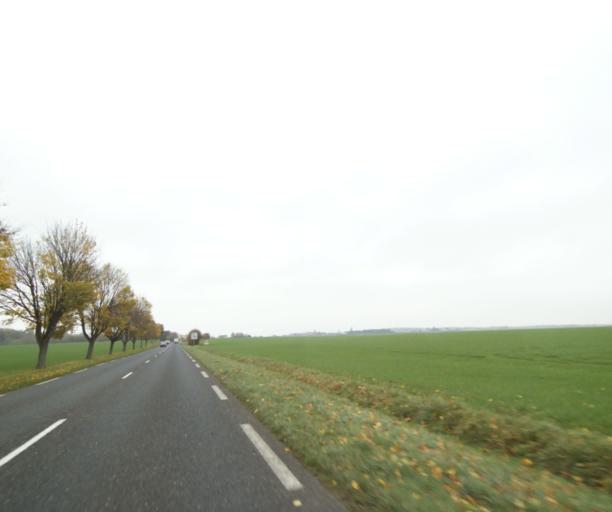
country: FR
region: Lorraine
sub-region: Departement de Meurthe-et-Moselle
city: Briey
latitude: 49.2776
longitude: 5.9594
